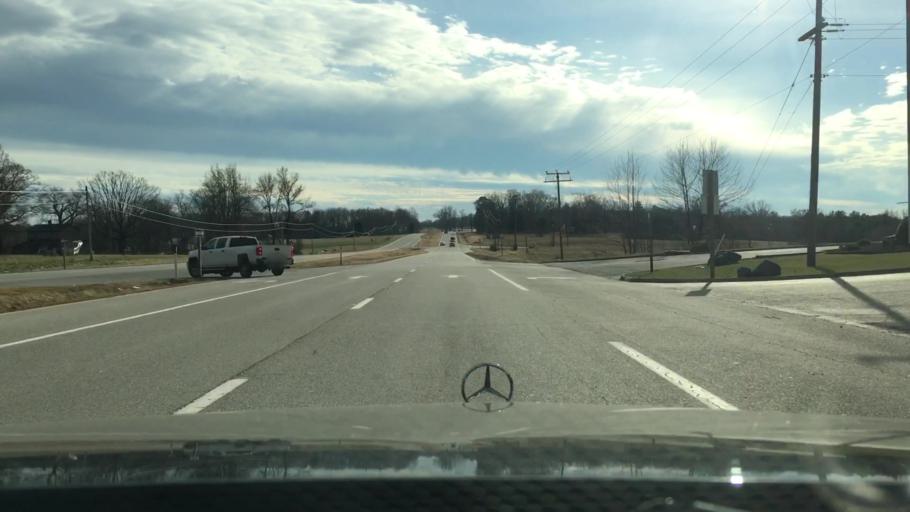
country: US
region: Virginia
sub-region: Pittsylvania County
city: Mount Hermon
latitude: 36.7327
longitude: -79.3823
